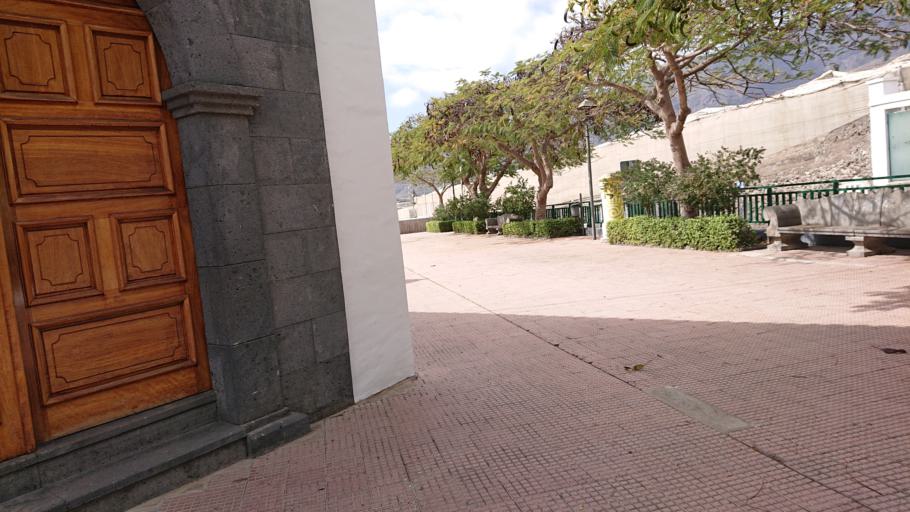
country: ES
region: Canary Islands
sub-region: Provincia de Santa Cruz de Tenerife
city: Los Llanos de Aridane
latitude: 28.6602
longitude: -17.9048
